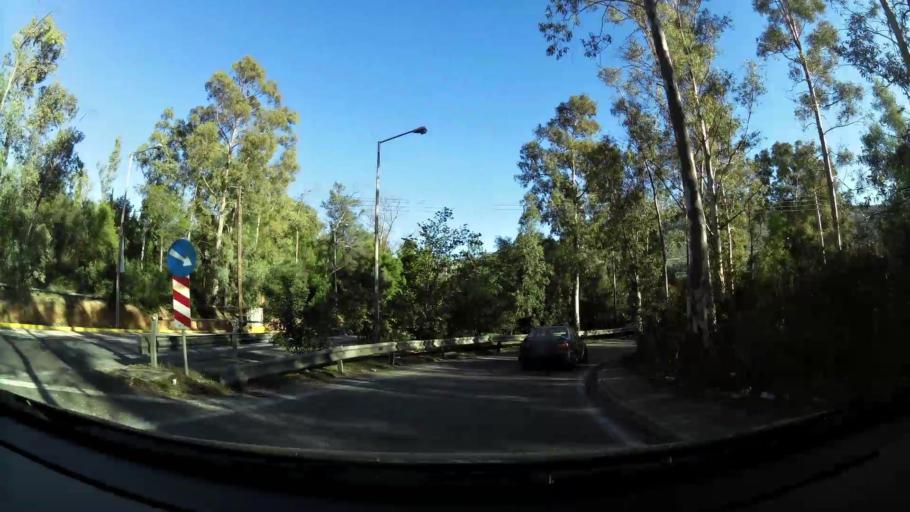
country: GR
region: Attica
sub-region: Nomarchia Athinas
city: Skaramangas
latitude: 38.0132
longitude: 23.6055
